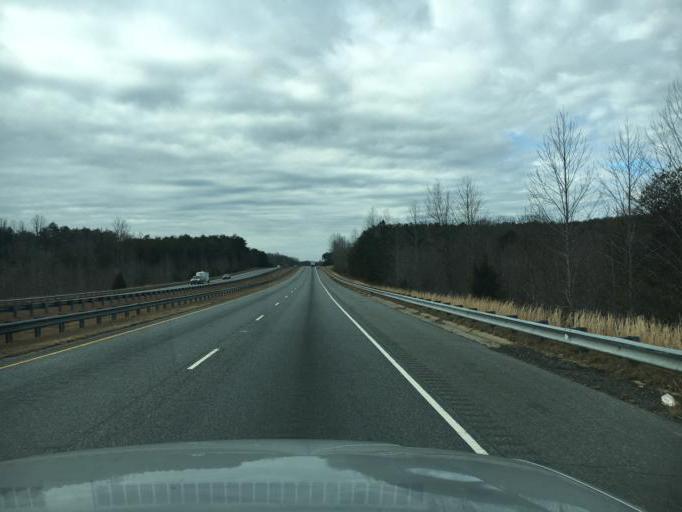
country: US
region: North Carolina
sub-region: Rutherford County
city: Spindale
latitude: 35.3038
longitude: -81.9608
